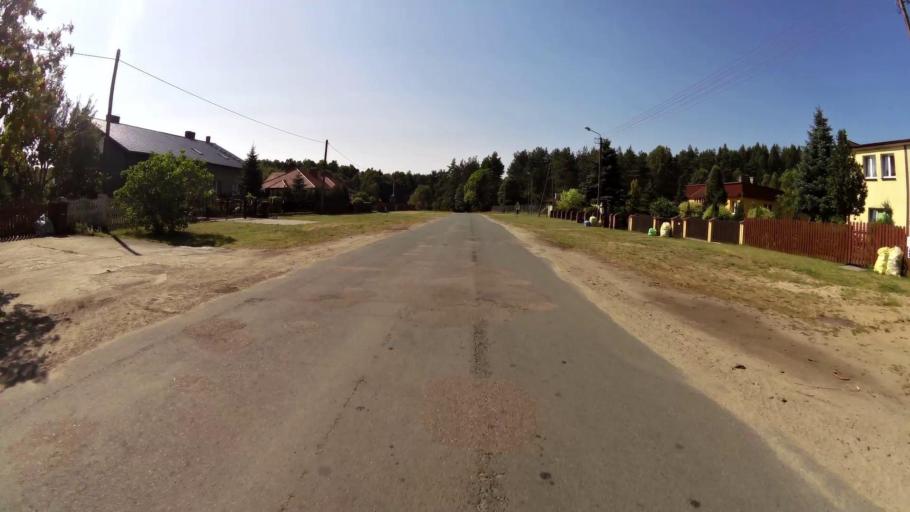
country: PL
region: West Pomeranian Voivodeship
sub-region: Powiat drawski
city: Czaplinek
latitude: 53.4338
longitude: 16.2678
